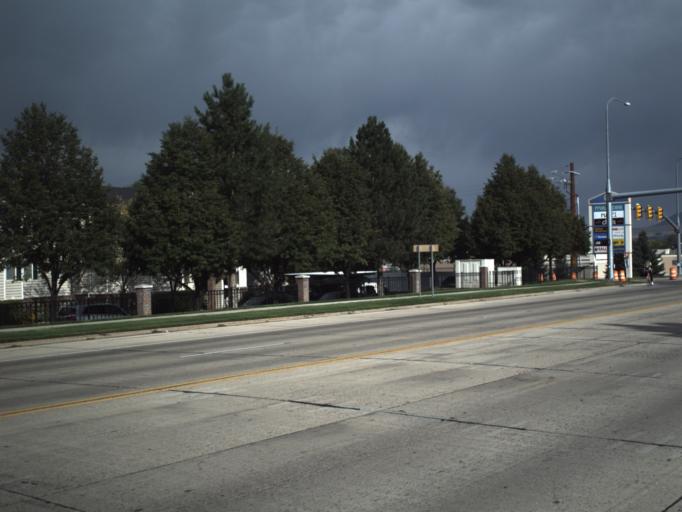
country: US
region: Utah
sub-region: Weber County
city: Harrisville
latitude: 41.2659
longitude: -111.9694
